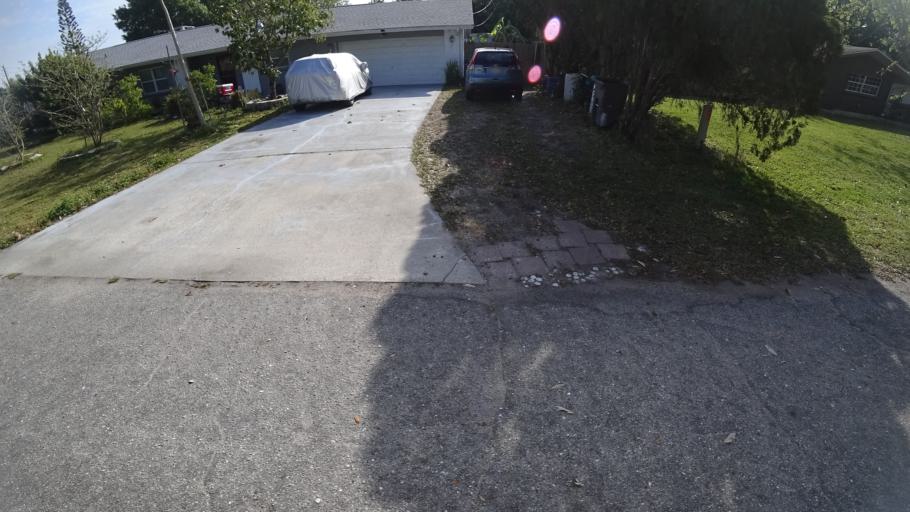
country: US
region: Florida
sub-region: Manatee County
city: Whitfield
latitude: 27.4247
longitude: -82.5524
